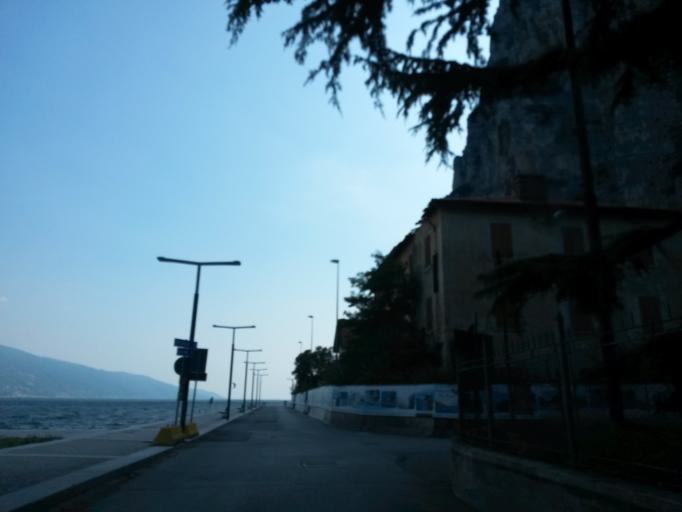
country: IT
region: Lombardy
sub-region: Provincia di Brescia
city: Pieve
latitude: 45.7526
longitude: 10.7504
